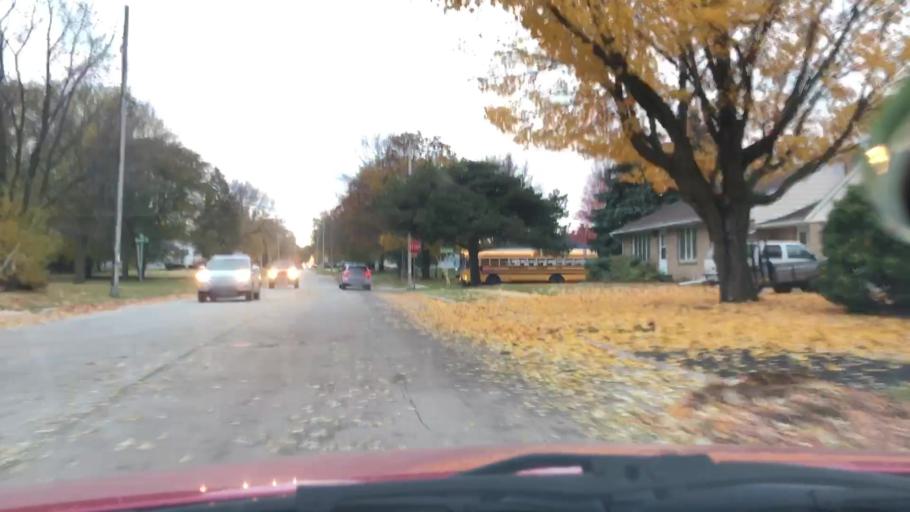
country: US
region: Wisconsin
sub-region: Outagamie County
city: Seymour
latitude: 44.5049
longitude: -88.3320
